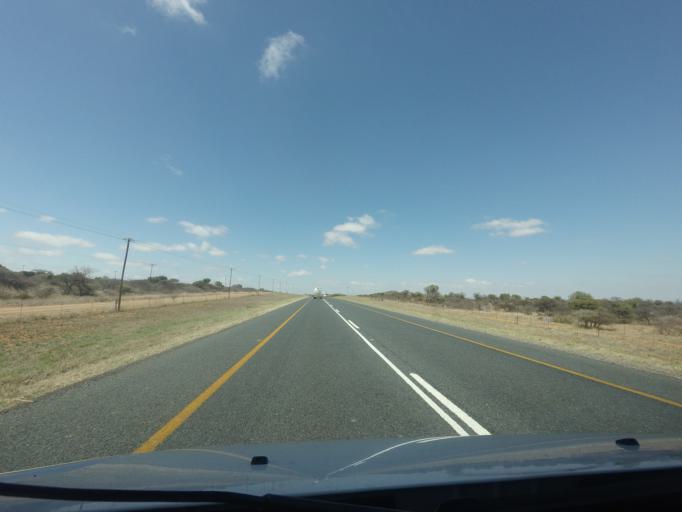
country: ZA
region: Limpopo
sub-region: Vhembe District Municipality
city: Louis Trichardt
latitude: -23.4220
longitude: 29.7511
